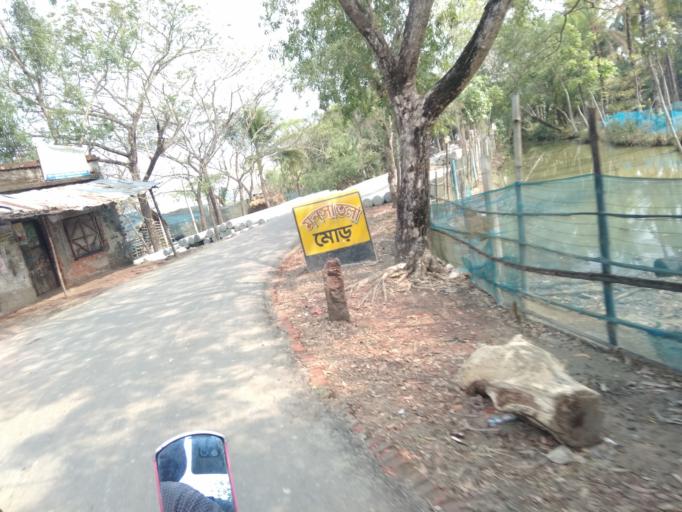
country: IN
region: West Bengal
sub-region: North 24 Parganas
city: Gosaba
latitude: 22.2306
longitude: 89.1565
